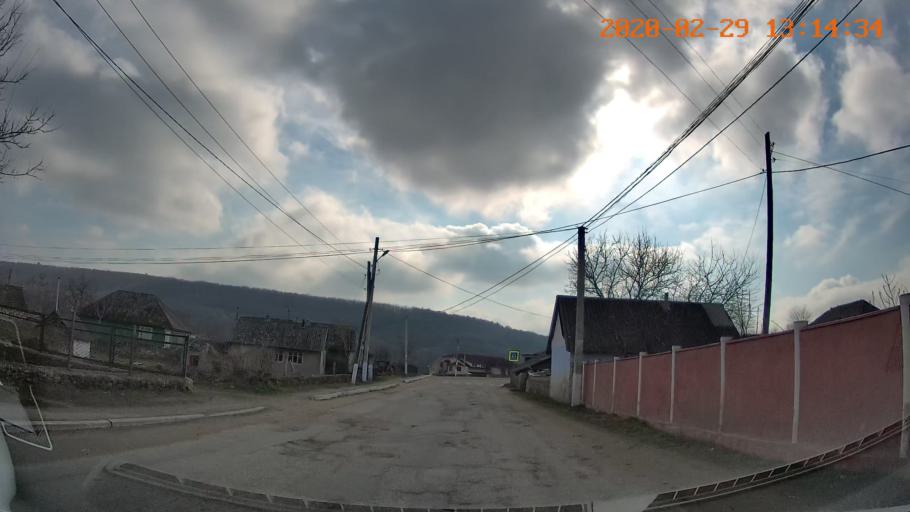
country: MD
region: Telenesti
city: Camenca
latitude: 48.0121
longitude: 28.6761
